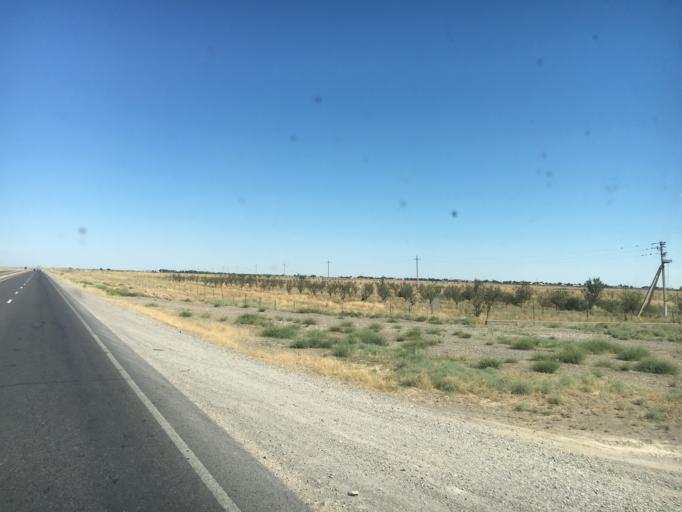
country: KZ
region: Ongtustik Qazaqstan
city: Turkestan
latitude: 43.5100
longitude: 67.8261
